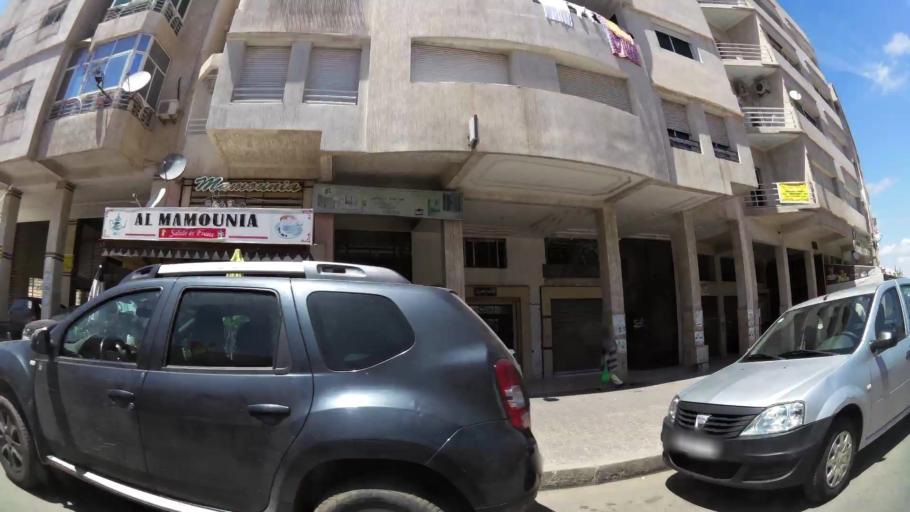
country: MA
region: Fes-Boulemane
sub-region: Fes
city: Fes
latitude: 34.0176
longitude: -4.9886
